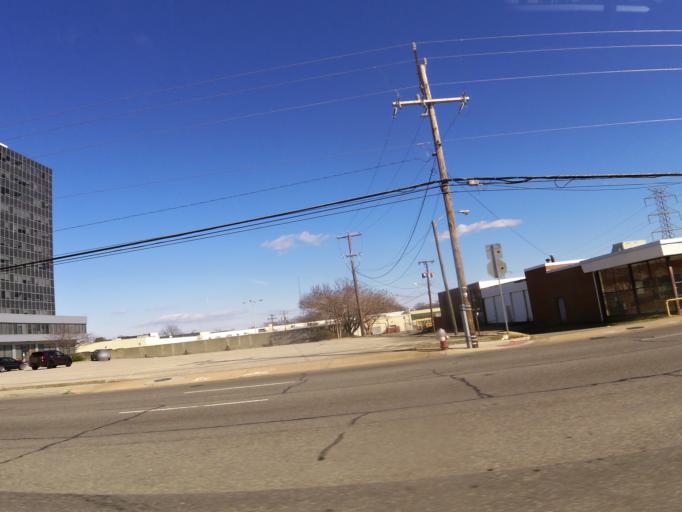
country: US
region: Virginia
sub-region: City of Newport News
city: Newport News
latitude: 37.0179
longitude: -76.4436
